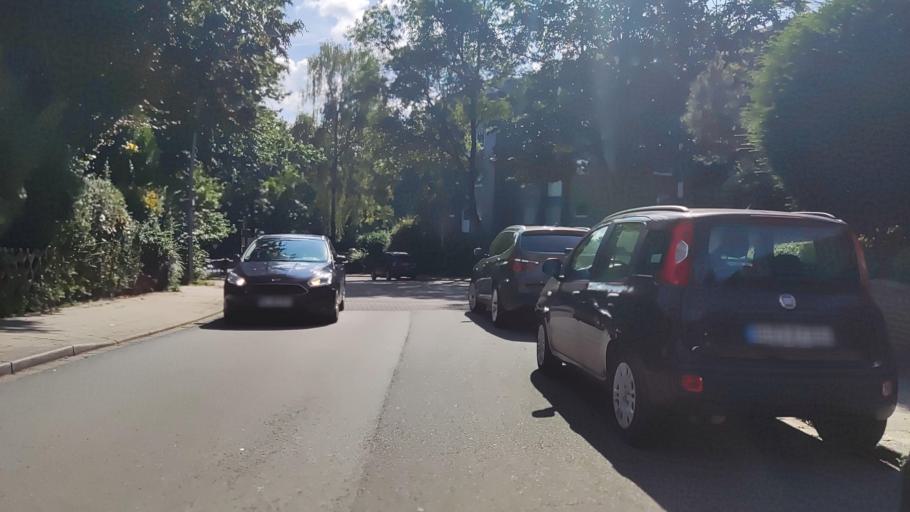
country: DE
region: North Rhine-Westphalia
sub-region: Regierungsbezirk Arnsberg
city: Bochum
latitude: 51.4590
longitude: 7.2542
